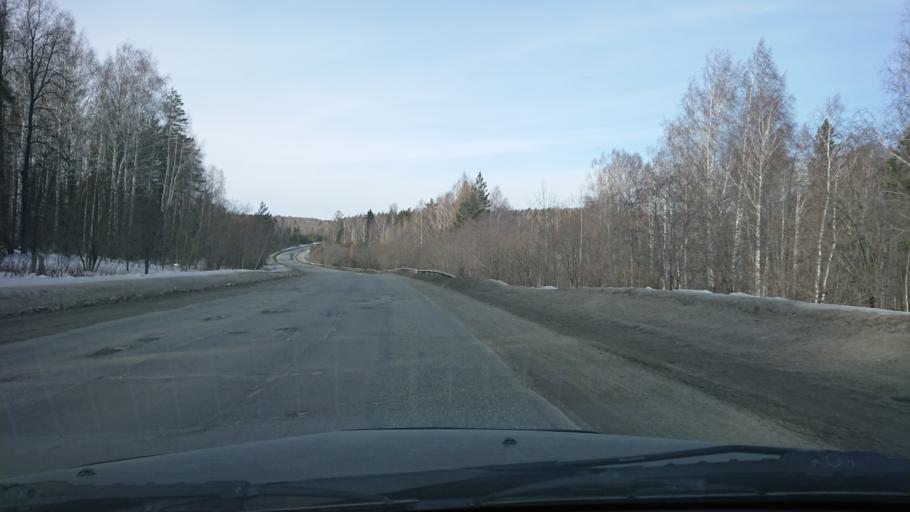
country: RU
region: Sverdlovsk
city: Degtyarsk
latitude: 56.7616
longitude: 60.0408
